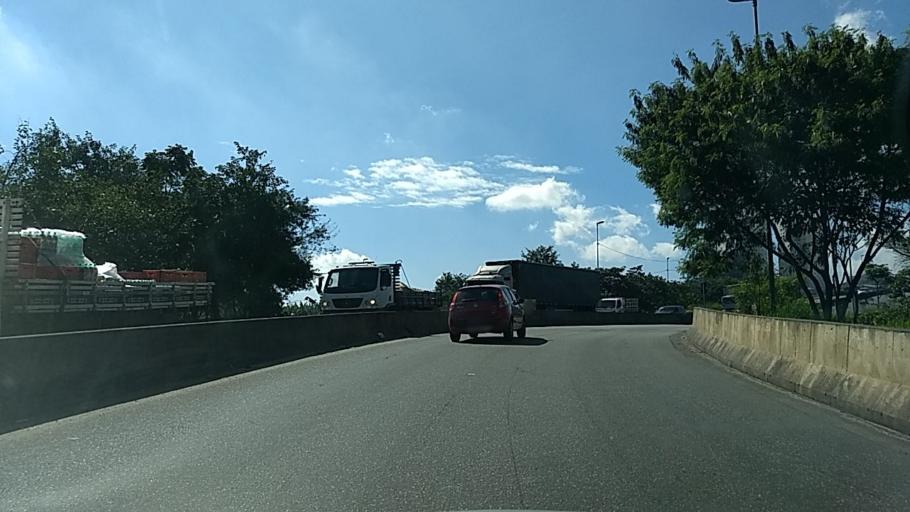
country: BR
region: Sao Paulo
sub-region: Guarulhos
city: Guarulhos
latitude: -23.4878
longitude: -46.5614
